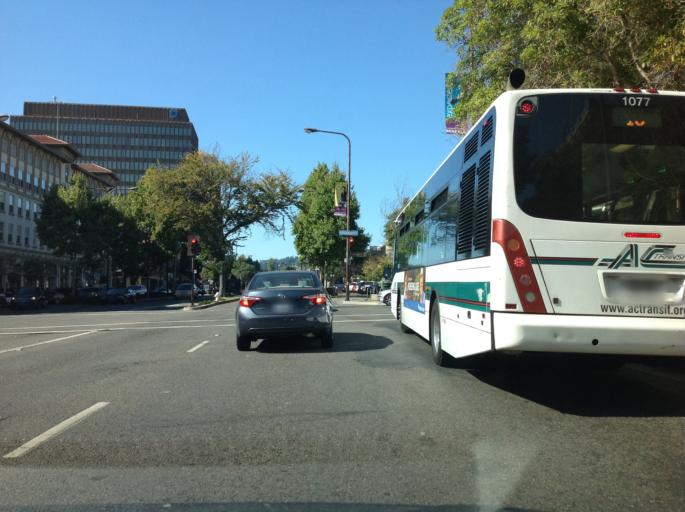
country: US
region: California
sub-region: Alameda County
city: Berkeley
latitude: 37.8683
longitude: -122.2677
